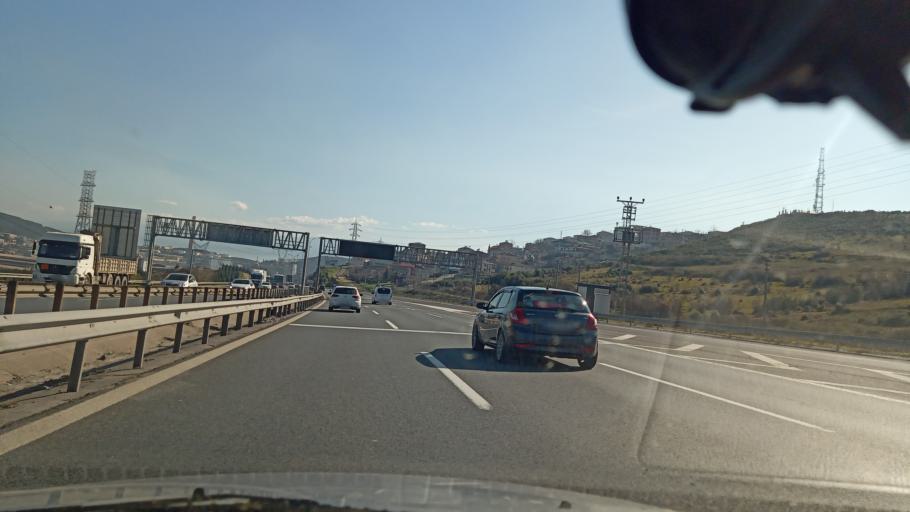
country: TR
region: Kocaeli
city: Tavsanli
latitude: 40.7864
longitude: 29.5231
